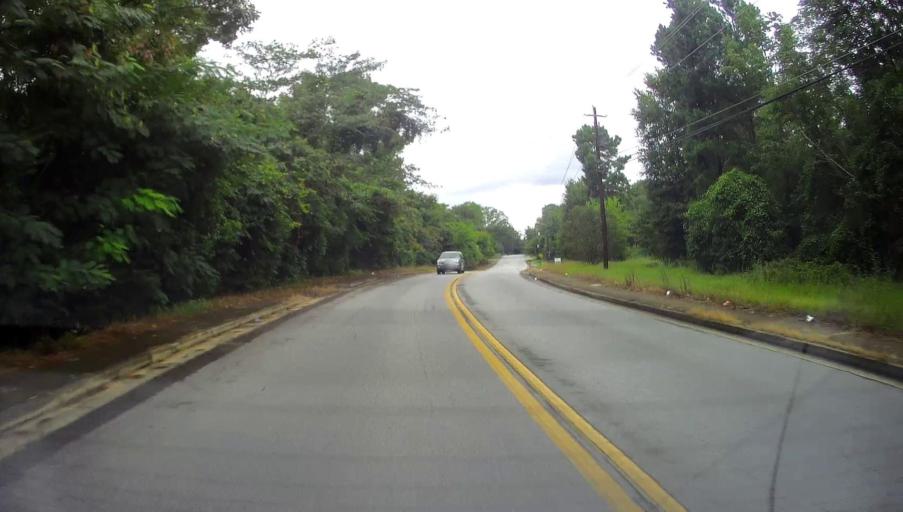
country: US
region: Georgia
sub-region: Bibb County
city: Macon
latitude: 32.7943
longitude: -83.6967
